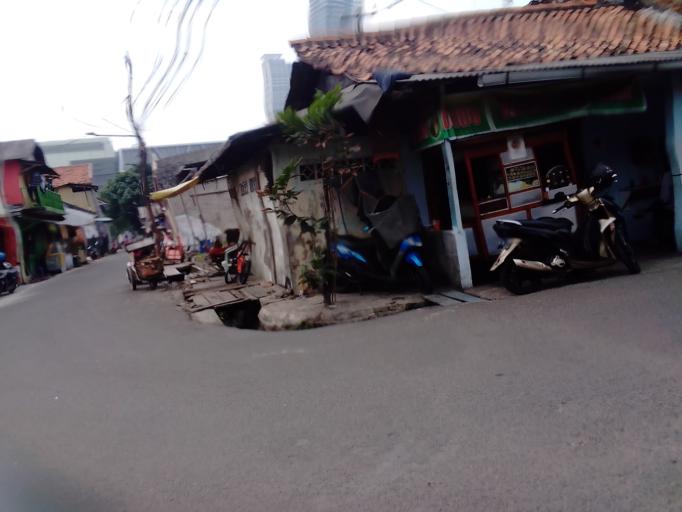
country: ID
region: Jakarta Raya
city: Jakarta
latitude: -6.1990
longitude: 106.8193
